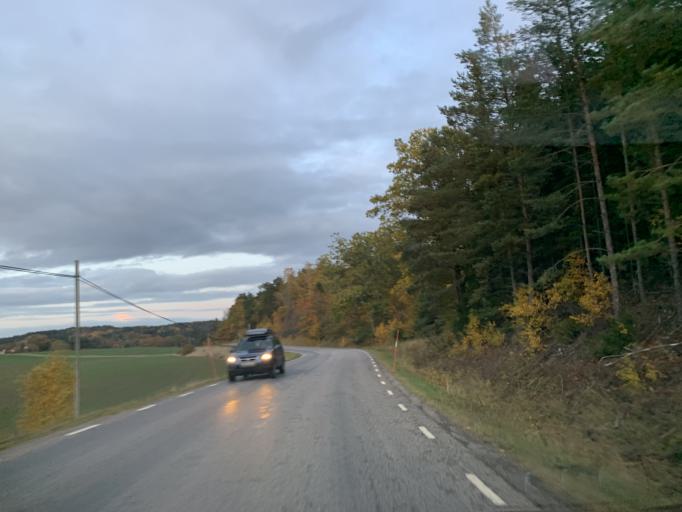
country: SE
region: Stockholm
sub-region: Nynashamns Kommun
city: Osmo
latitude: 58.9485
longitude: 17.7631
